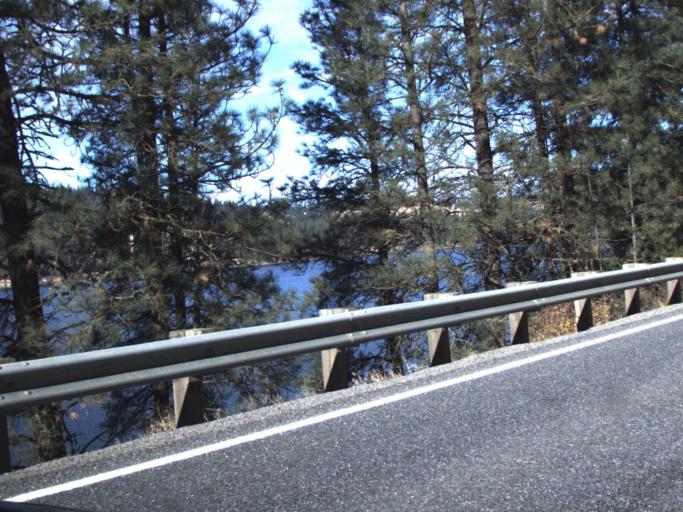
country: US
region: Washington
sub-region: Stevens County
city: Kettle Falls
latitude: 48.2192
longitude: -118.1739
